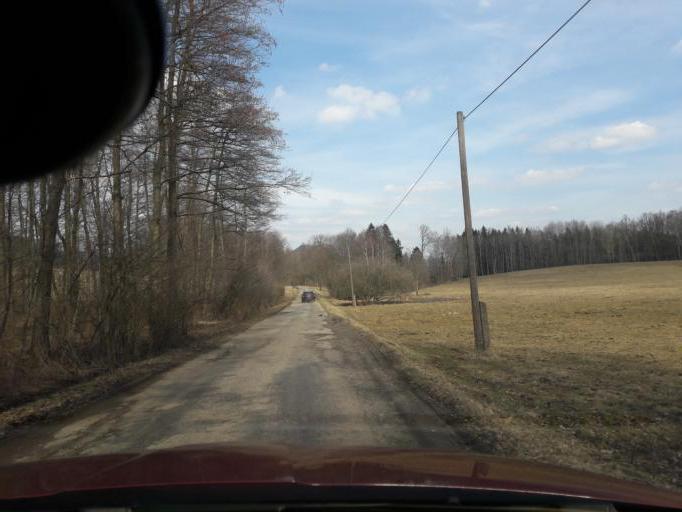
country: CZ
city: Zakupy
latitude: 50.7222
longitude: 14.6188
